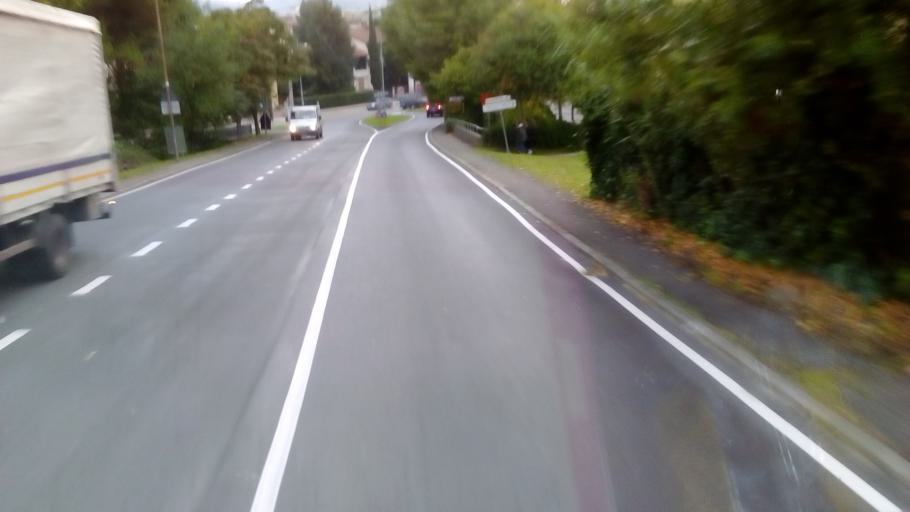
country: IT
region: Tuscany
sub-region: Province of Florence
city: Castelfiorentino
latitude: 43.6117
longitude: 10.9695
